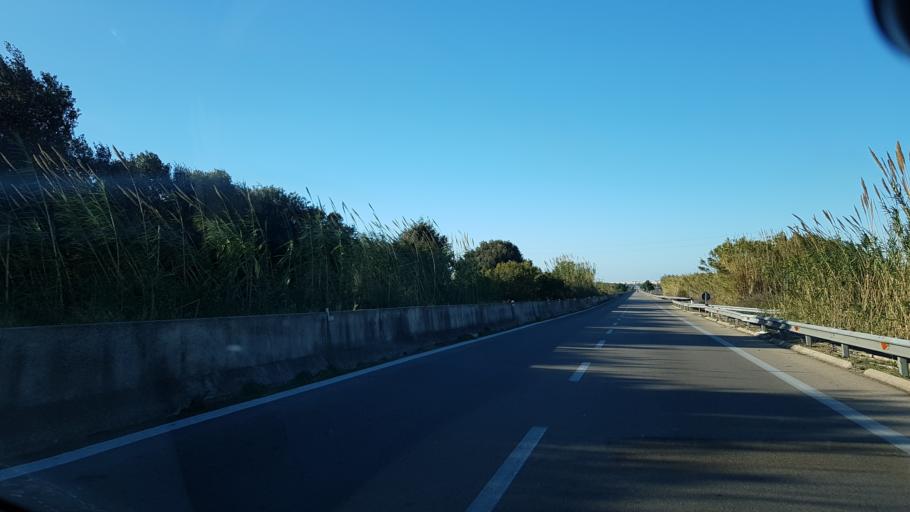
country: IT
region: Apulia
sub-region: Provincia di Lecce
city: Alezio
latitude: 40.0163
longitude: 18.0469
